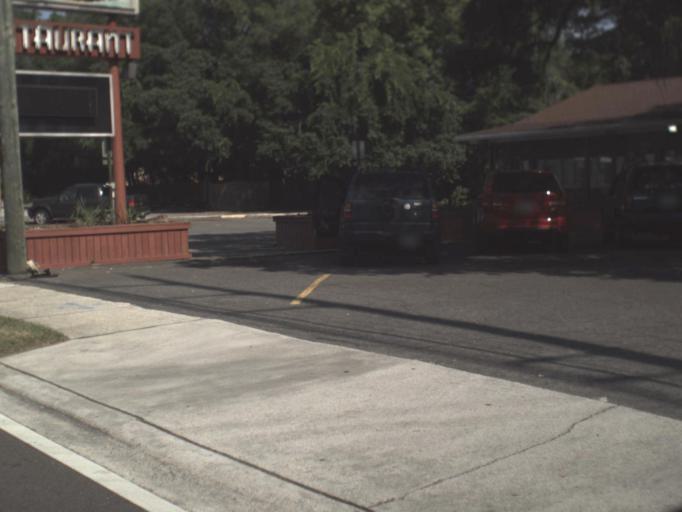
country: US
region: Florida
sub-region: Clay County
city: Bellair-Meadowbrook Terrace
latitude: 30.2821
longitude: -81.7467
